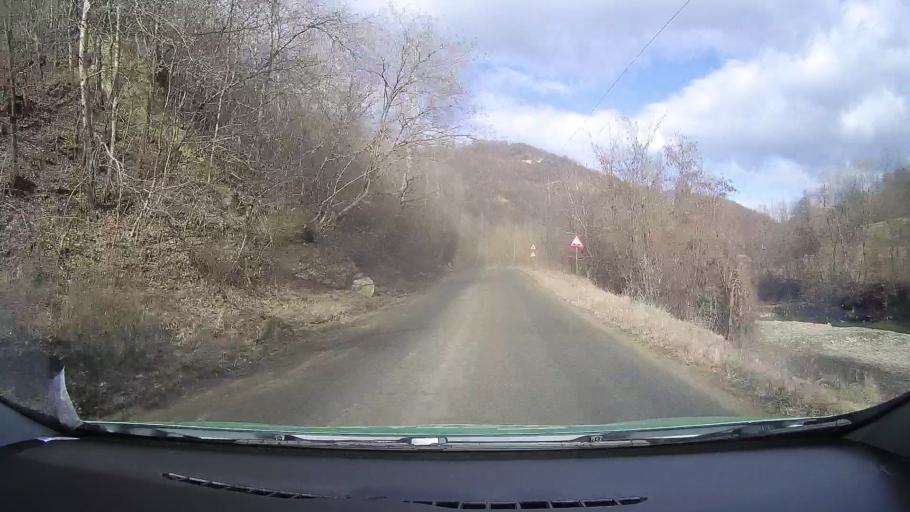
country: RO
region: Dambovita
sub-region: Oras Pucioasa
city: Pucioasa
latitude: 45.1001
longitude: 25.4422
